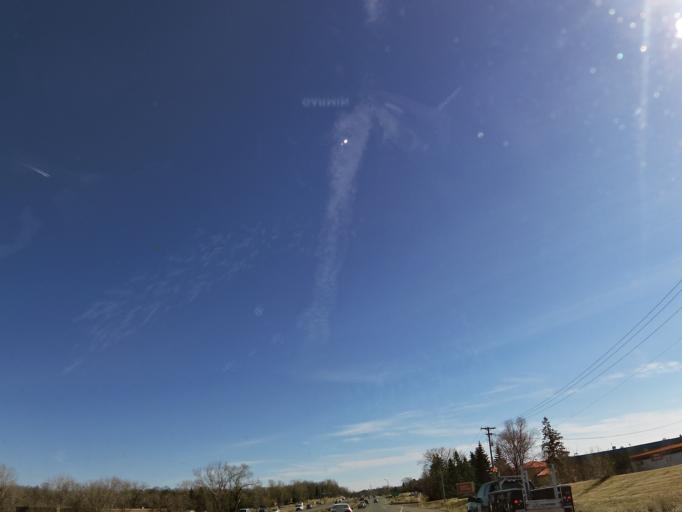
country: US
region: Minnesota
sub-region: Hennepin County
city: Plymouth
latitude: 45.0057
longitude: -93.4467
